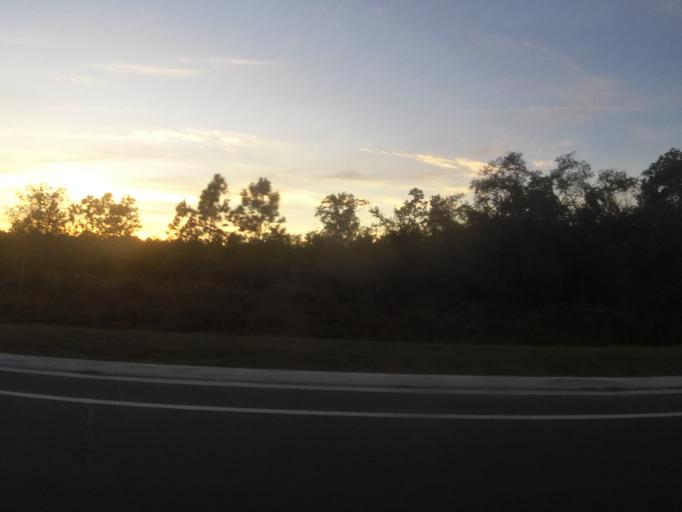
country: US
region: Florida
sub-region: Saint Johns County
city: Fruit Cove
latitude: 30.0955
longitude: -81.5228
